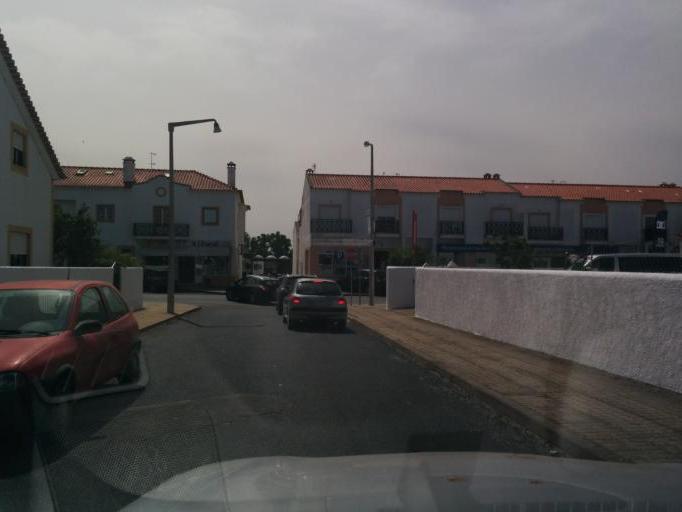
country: PT
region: Beja
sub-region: Odemira
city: Vila Nova de Milfontes
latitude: 37.7297
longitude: -8.7767
